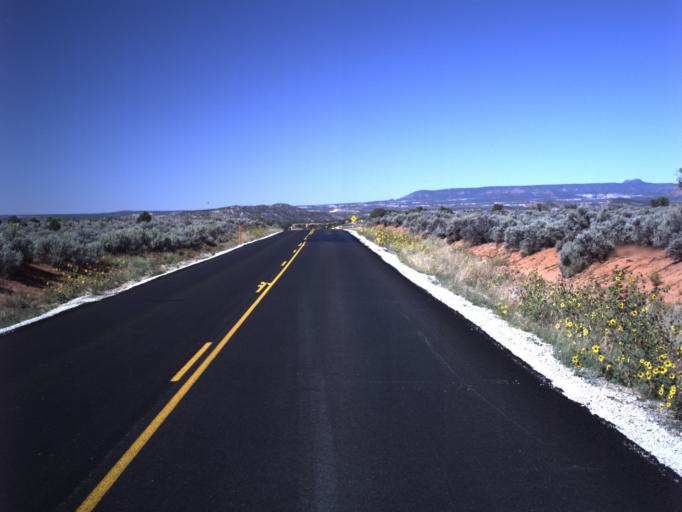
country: US
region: Utah
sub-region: San Juan County
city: Blanding
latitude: 37.5747
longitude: -109.5455
